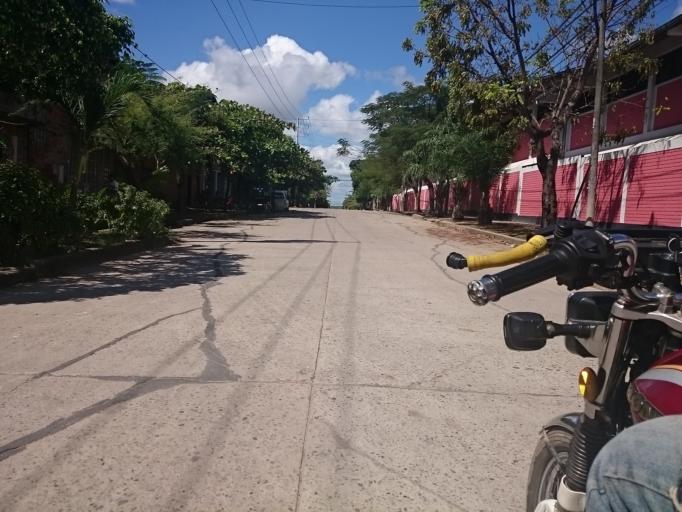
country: PE
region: Ucayali
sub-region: Provincia de Coronel Portillo
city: Pucallpa
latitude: -8.3796
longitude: -74.5291
